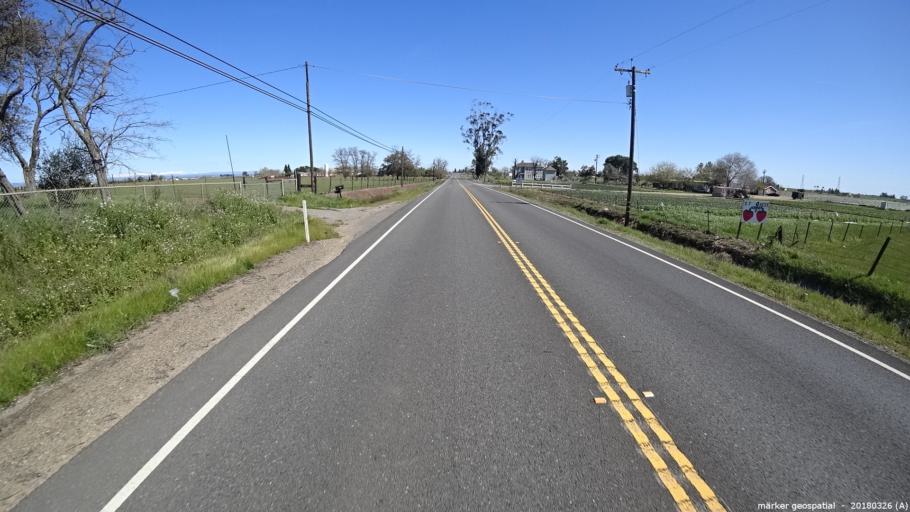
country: US
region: California
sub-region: Sacramento County
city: Rosemont
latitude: 38.5216
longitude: -121.3079
